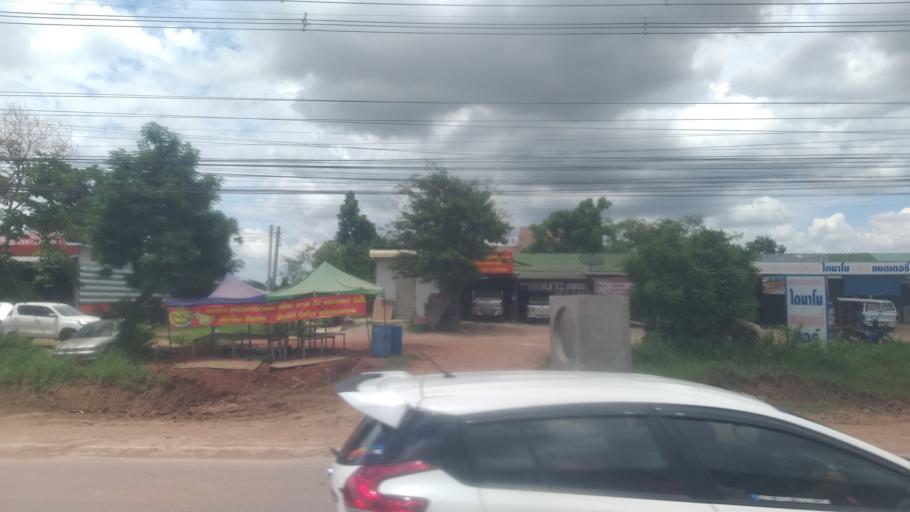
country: TH
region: Nakhon Ratchasima
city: Nakhon Ratchasima
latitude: 15.0664
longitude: 102.1215
